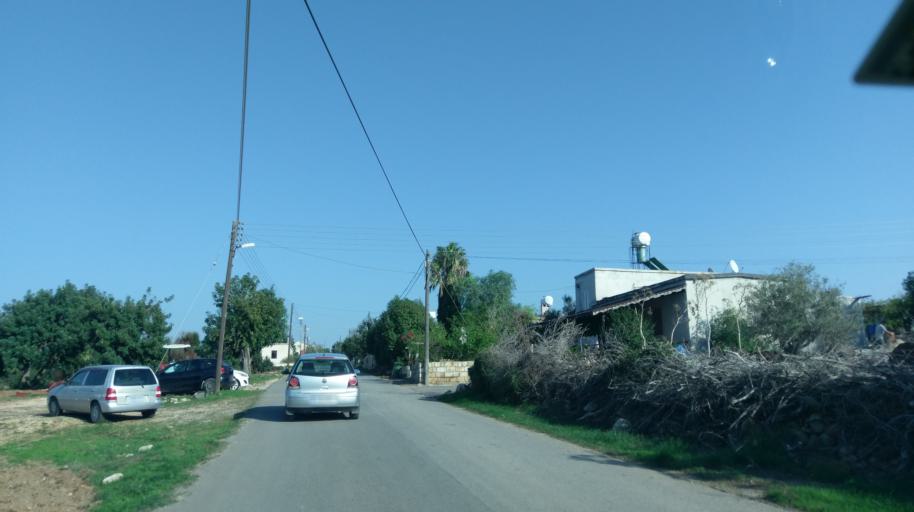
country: CY
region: Ammochostos
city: Leonarisso
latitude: 35.5350
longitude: 34.1955
